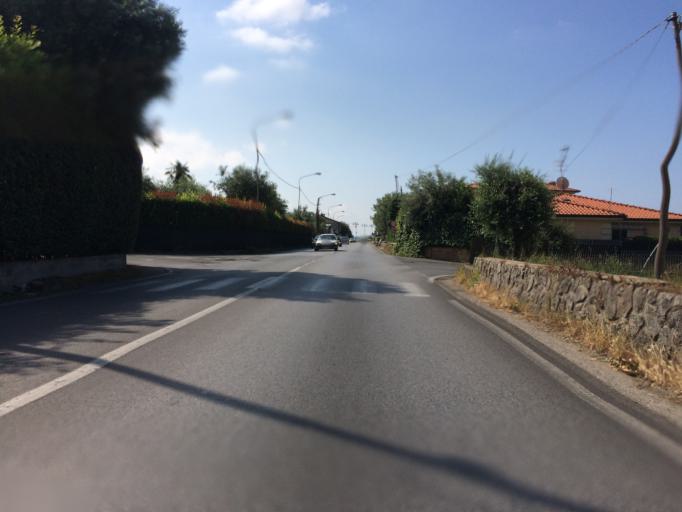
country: IT
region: Tuscany
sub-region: Provincia di Massa-Carrara
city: Capanne-Prato-Cinquale
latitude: 44.0103
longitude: 10.1591
